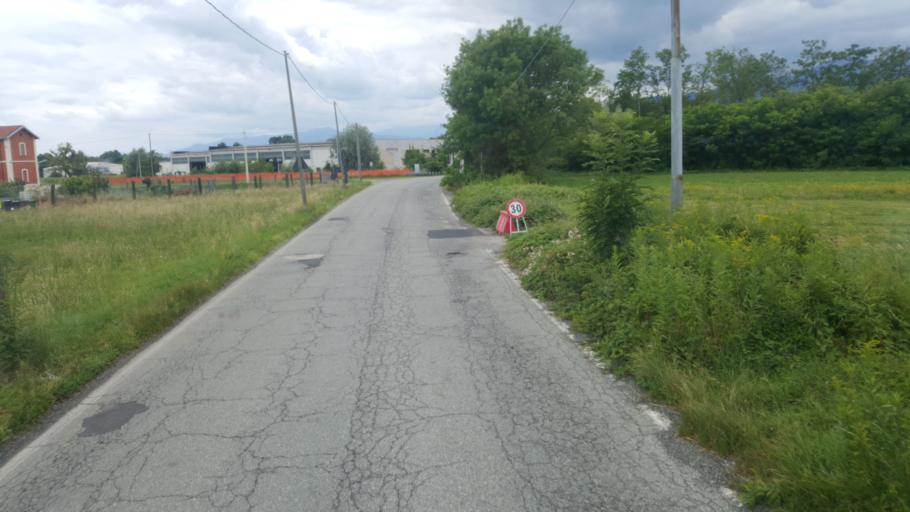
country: IT
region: Piedmont
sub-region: Provincia di Torino
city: San Ponso
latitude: 45.3521
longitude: 7.6800
